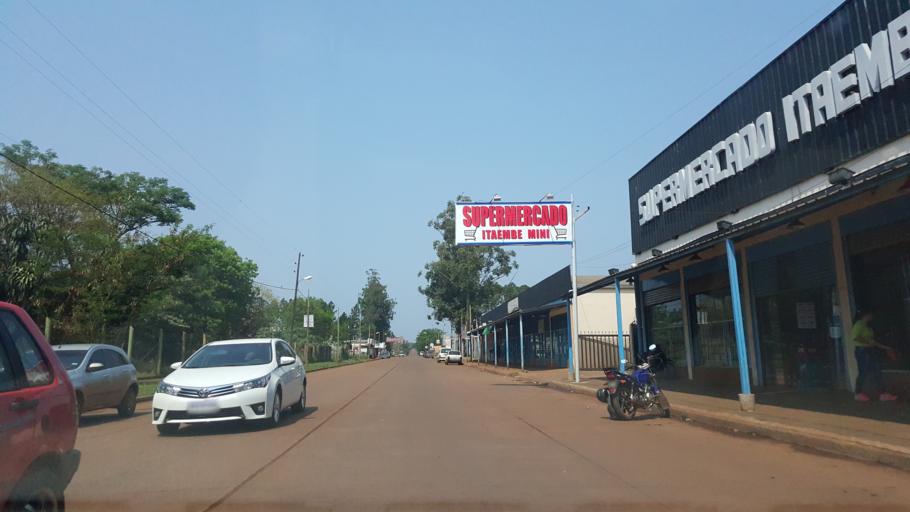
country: AR
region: Misiones
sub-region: Departamento de Capital
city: Posadas
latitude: -27.4148
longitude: -55.9562
